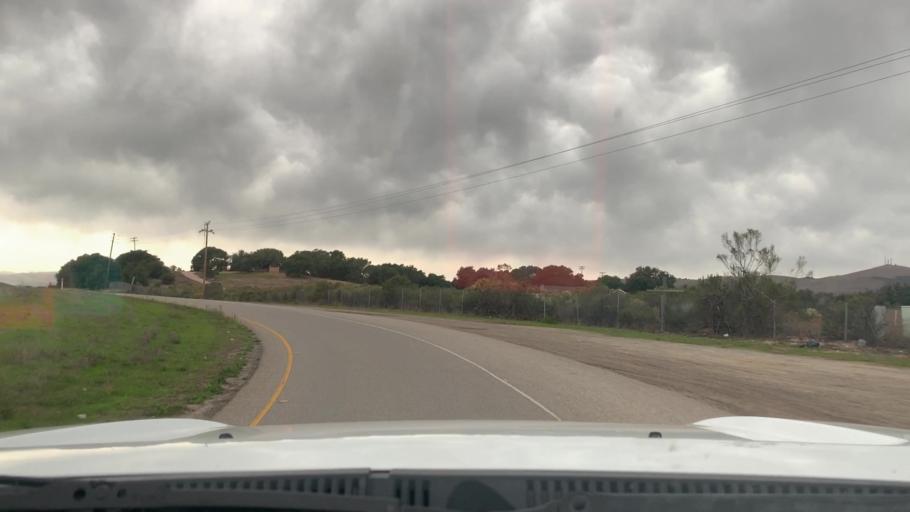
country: US
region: California
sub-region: San Luis Obispo County
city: Nipomo
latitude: 35.0726
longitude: -120.5150
